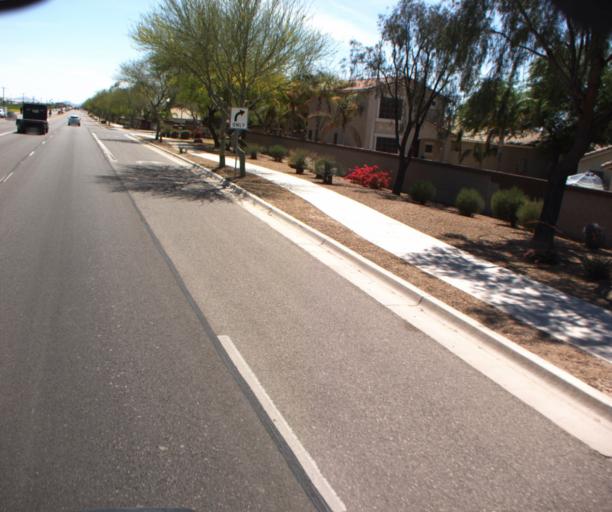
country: US
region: Arizona
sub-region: Maricopa County
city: Sun Lakes
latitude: 33.2303
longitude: -111.8414
